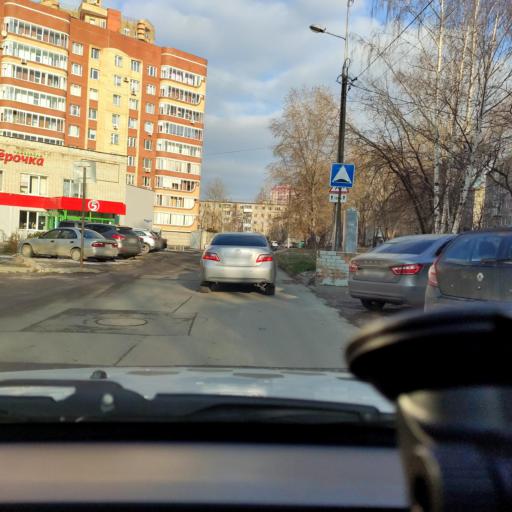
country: RU
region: Perm
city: Perm
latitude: 57.9969
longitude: 56.1945
